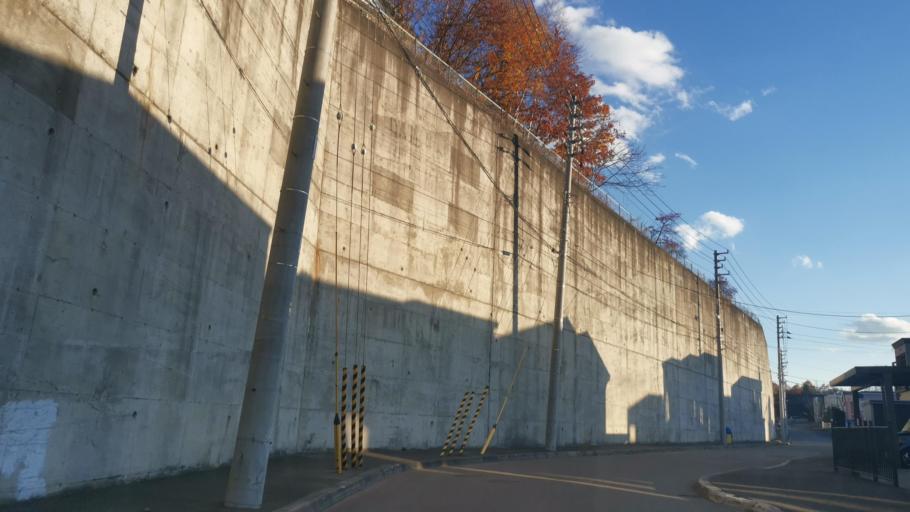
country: JP
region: Hokkaido
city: Sapporo
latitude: 42.9968
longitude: 141.3661
